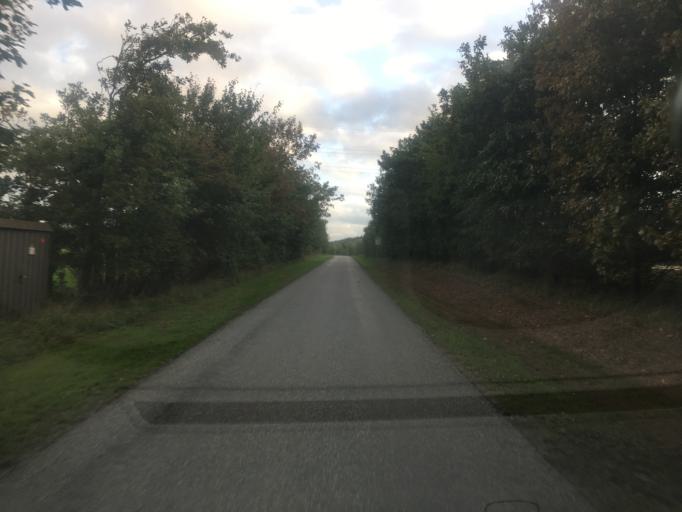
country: DK
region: South Denmark
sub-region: Tonder Kommune
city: Logumkloster
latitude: 55.0300
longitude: 8.9180
